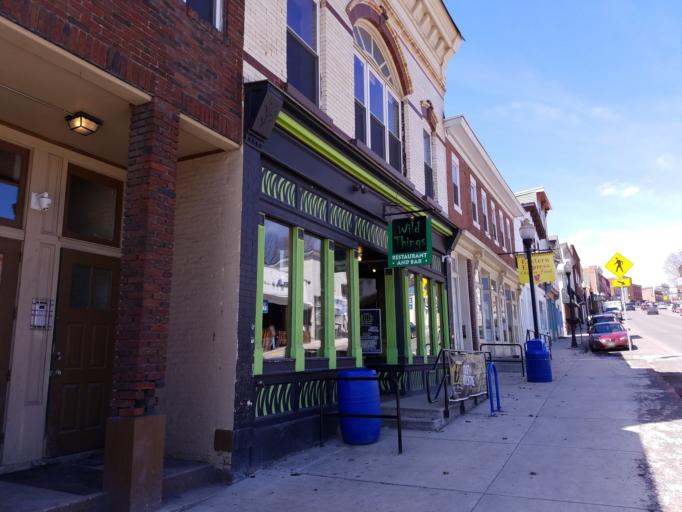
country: US
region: Maryland
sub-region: Allegany County
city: Frostburg
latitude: 39.6558
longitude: -78.9255
